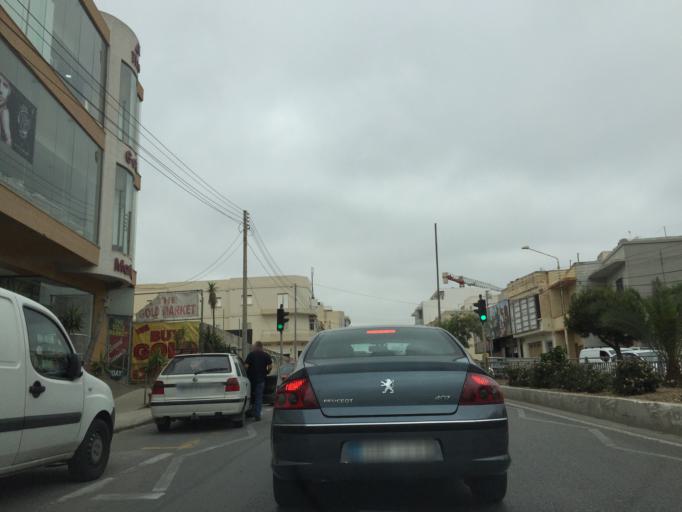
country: MT
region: Attard
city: Attard
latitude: 35.8892
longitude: 14.4393
